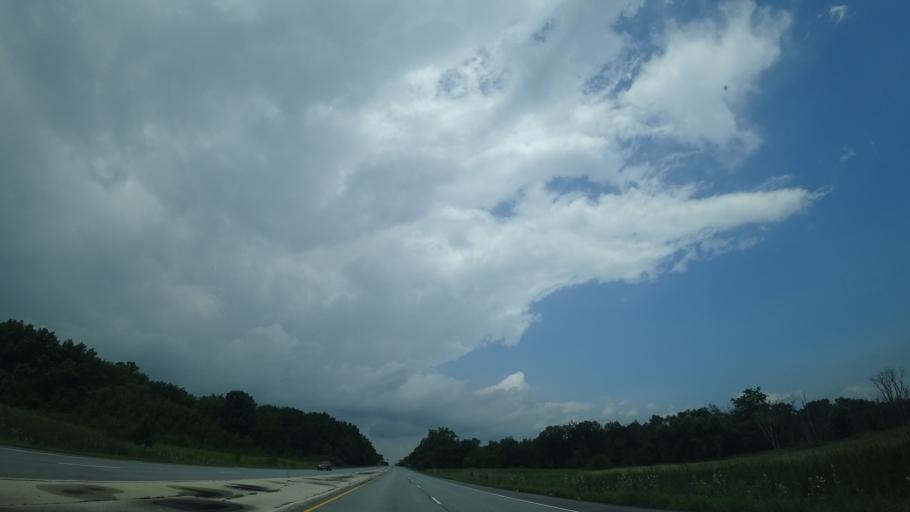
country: US
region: Illinois
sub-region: Cook County
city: Country Club Hills
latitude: 41.5382
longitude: -87.7326
